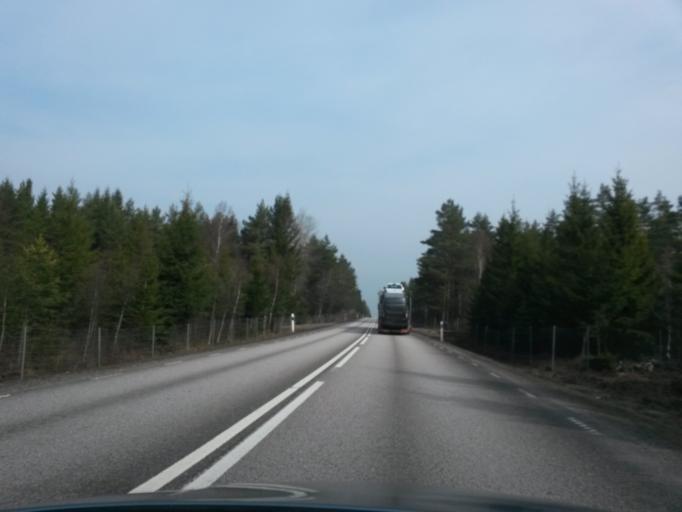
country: SE
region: Vaestra Goetaland
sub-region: Gullspangs Kommun
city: Hova
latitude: 58.8355
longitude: 14.1902
